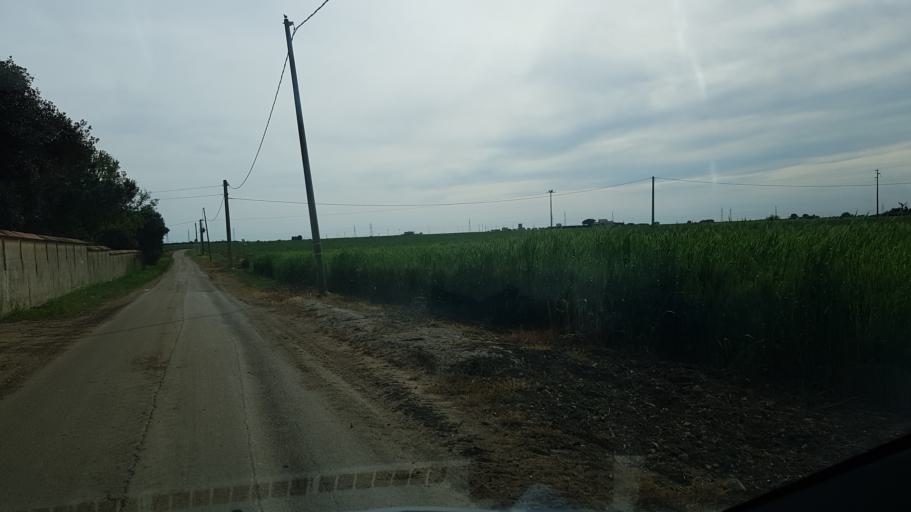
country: IT
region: Apulia
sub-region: Provincia di Brindisi
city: La Rosa
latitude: 40.5842
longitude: 17.9354
